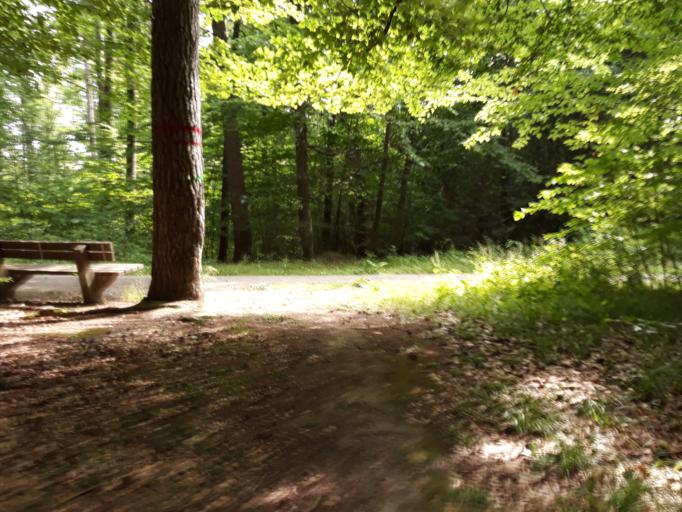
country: DE
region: Baden-Wuerttemberg
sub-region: Regierungsbezirk Stuttgart
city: Schonaich
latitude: 48.6730
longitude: 9.0425
